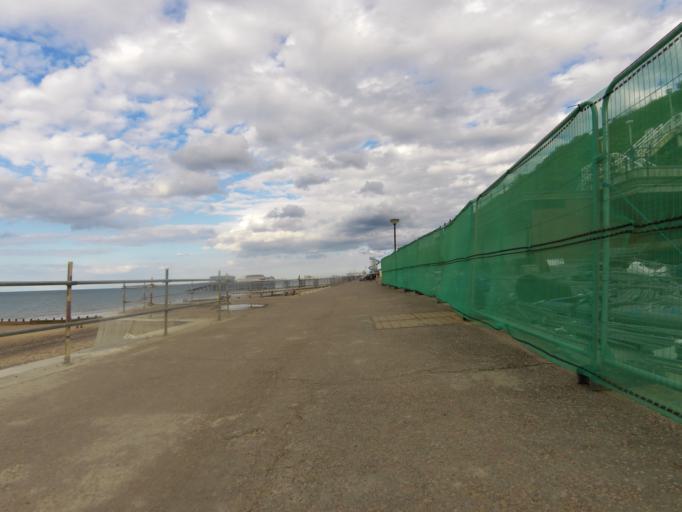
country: GB
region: England
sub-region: Norfolk
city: Cromer
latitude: 52.9337
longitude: 1.2950
